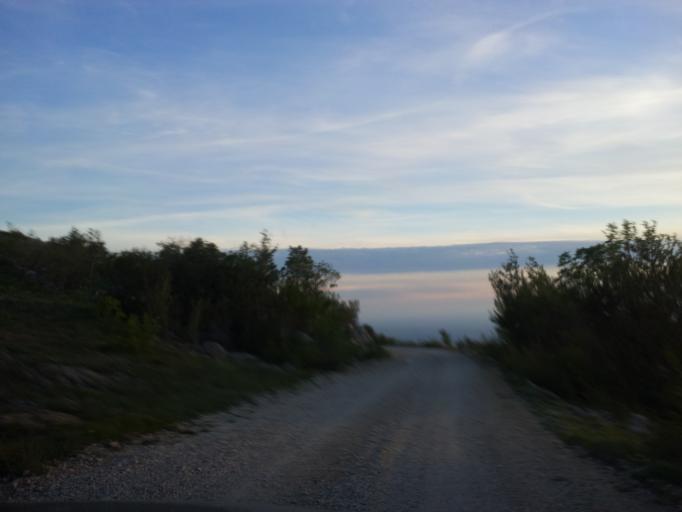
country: HR
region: Zadarska
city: Obrovac
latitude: 44.2566
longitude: 15.6337
